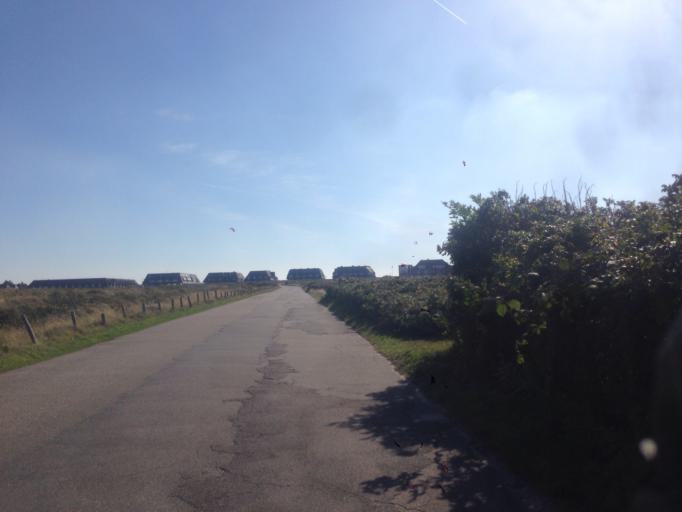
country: DE
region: Schleswig-Holstein
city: Westerland
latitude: 54.9607
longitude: 8.3340
